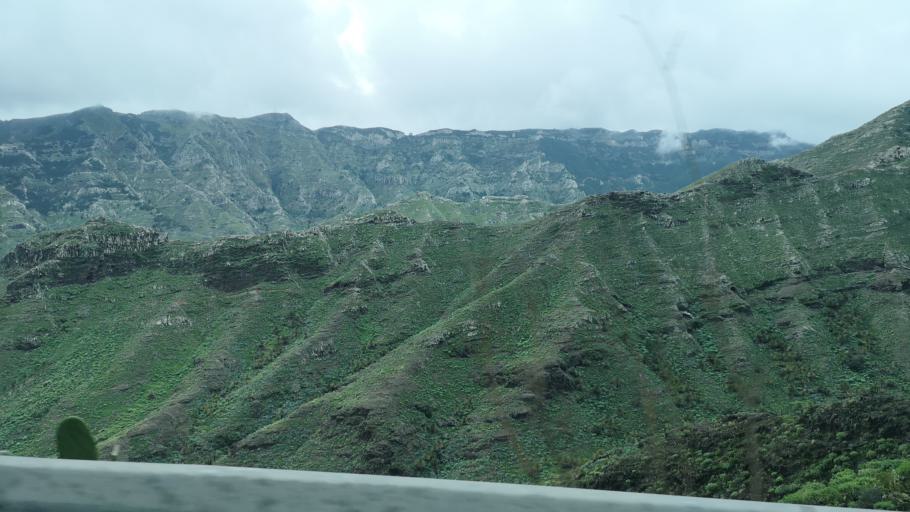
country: ES
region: Canary Islands
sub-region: Provincia de Santa Cruz de Tenerife
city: Hermigua
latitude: 28.1285
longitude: -17.1728
